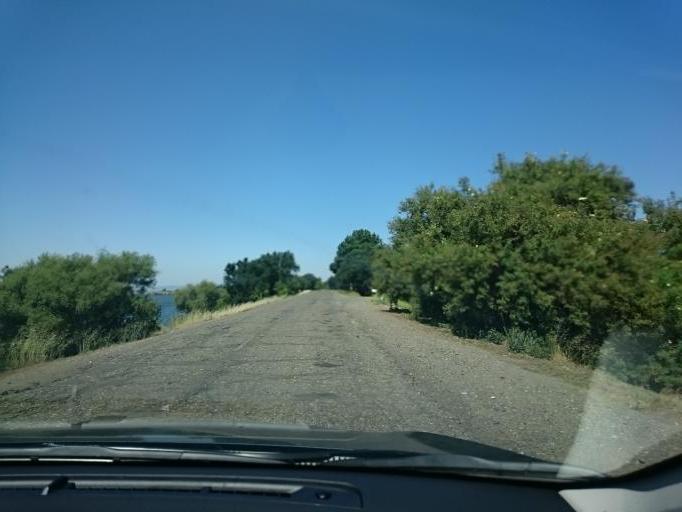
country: US
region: California
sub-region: Yolo County
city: West Sacramento
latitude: 38.5179
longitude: -121.5355
